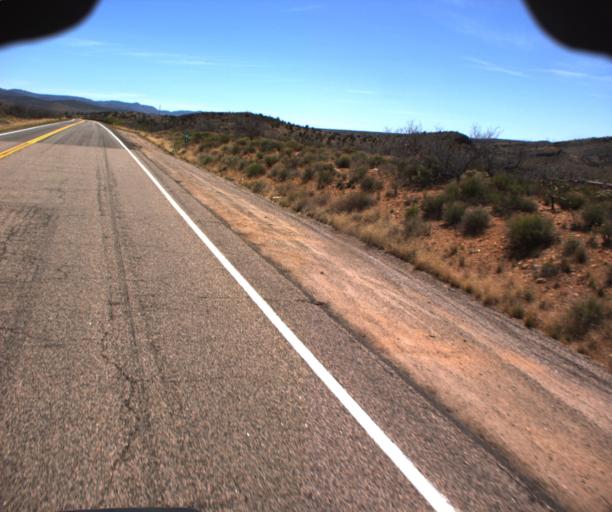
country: US
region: Arizona
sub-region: Mohave County
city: New Kingman-Butler
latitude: 35.3712
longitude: -113.7183
